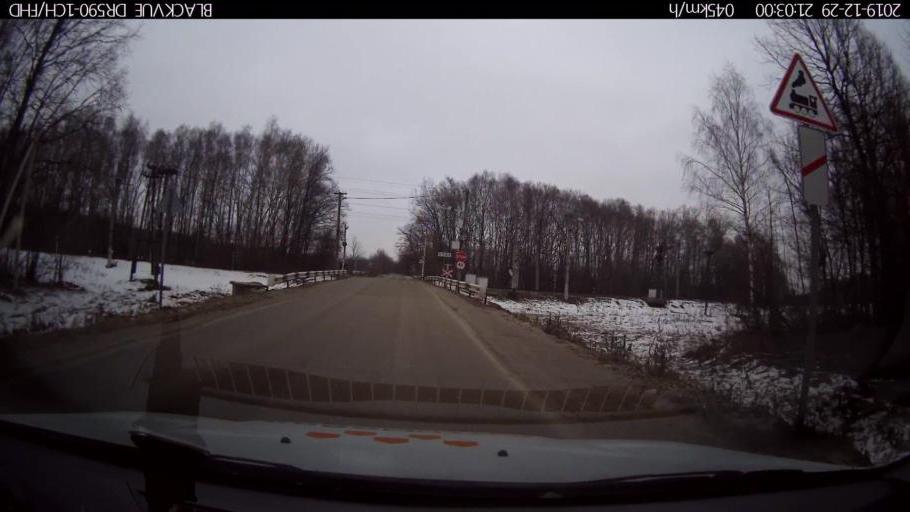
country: RU
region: Nizjnij Novgorod
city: Afonino
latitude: 56.1938
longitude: 44.0050
